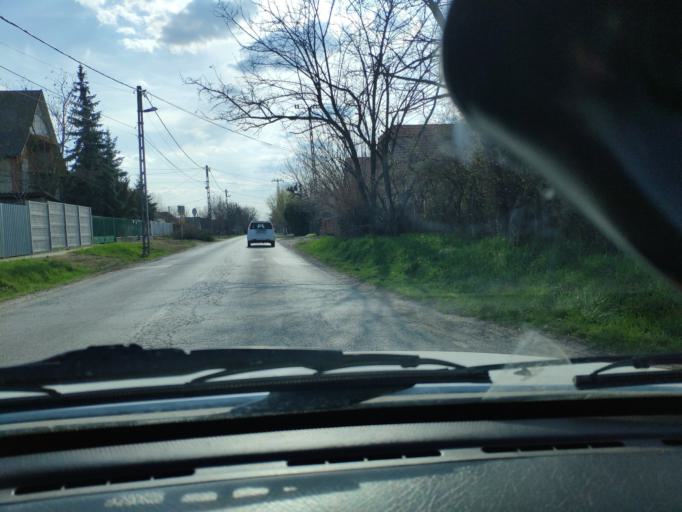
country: HU
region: Pest
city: Rackeve
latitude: 47.1556
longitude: 18.9271
